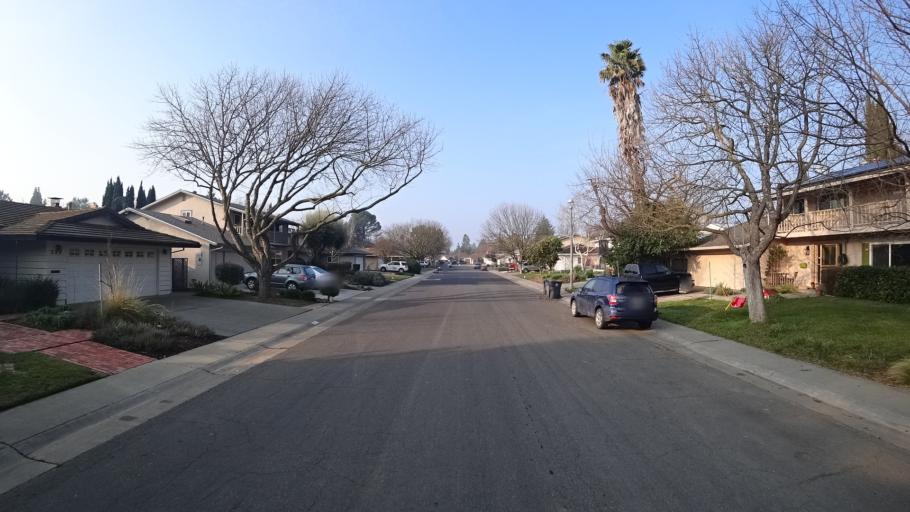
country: US
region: California
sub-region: Yolo County
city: Davis
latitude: 38.5646
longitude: -121.7502
